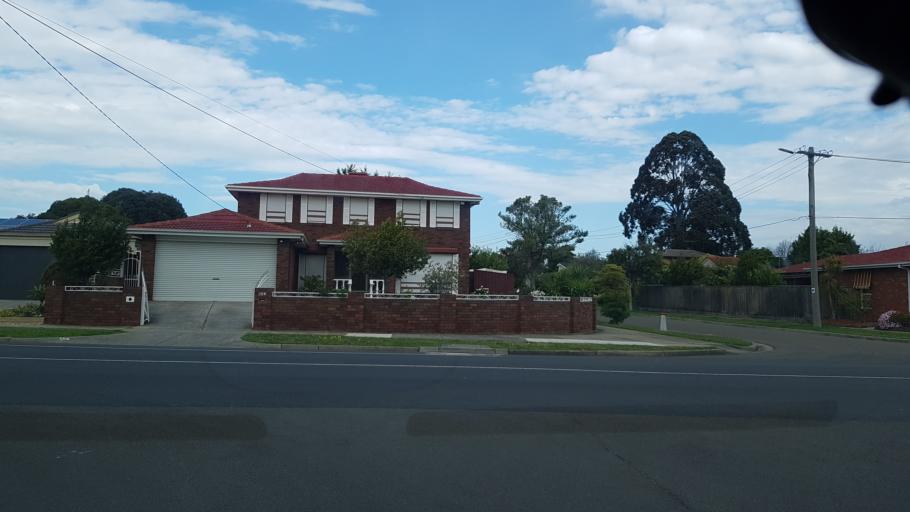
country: AU
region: Victoria
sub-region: Monash
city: Notting Hill
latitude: -37.9135
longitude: 145.1696
